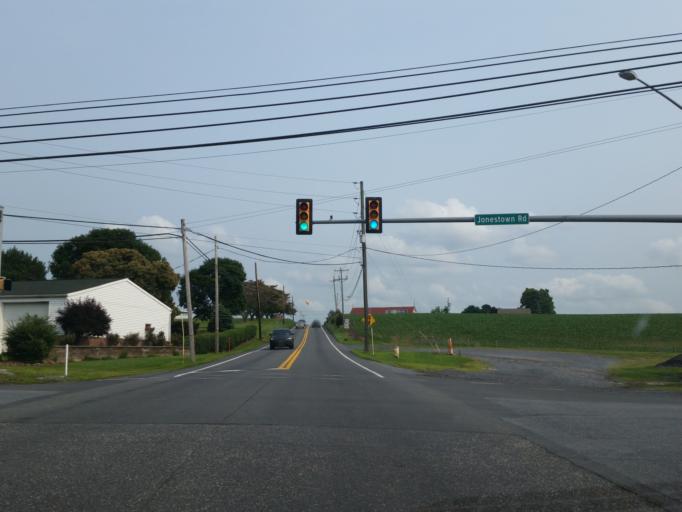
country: US
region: Pennsylvania
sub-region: Dauphin County
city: Skyline View
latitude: 40.3754
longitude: -76.6536
